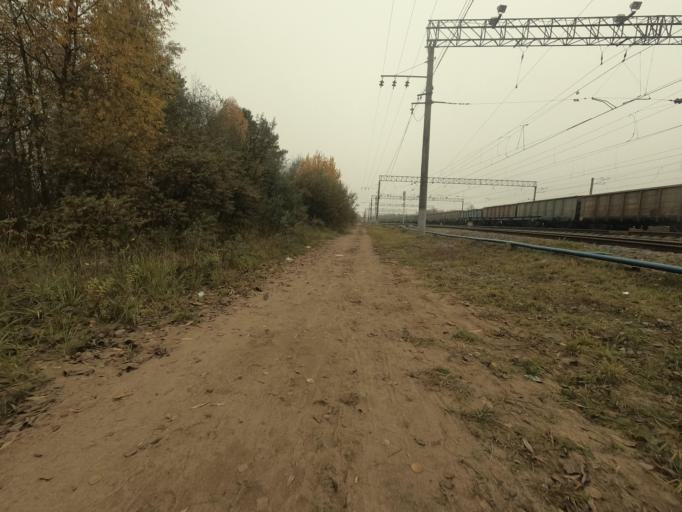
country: RU
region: Leningrad
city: Pavlovo
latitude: 59.7666
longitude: 30.9537
